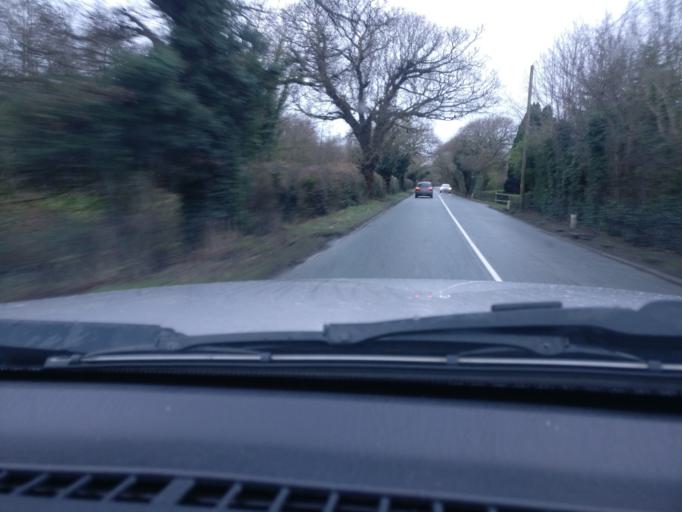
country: IE
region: Leinster
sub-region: An Mhi
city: Longwood
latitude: 53.4930
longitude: -6.8638
